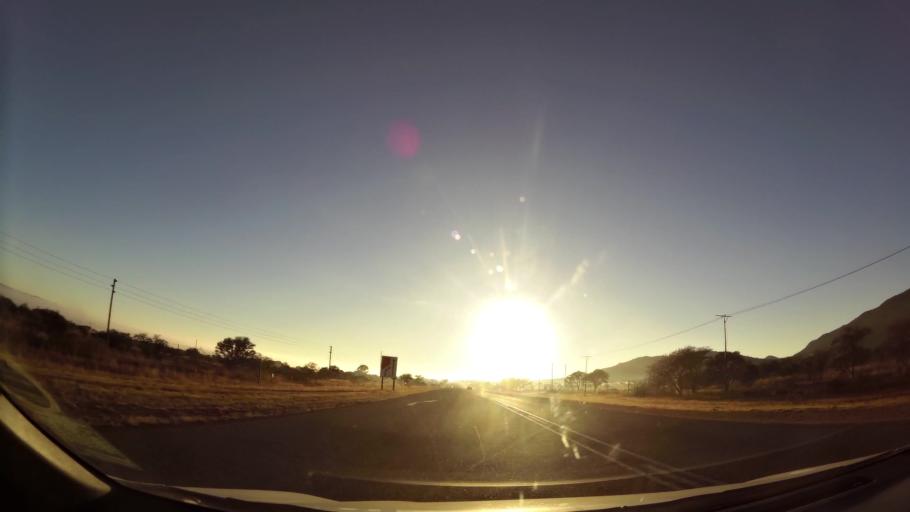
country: ZA
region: Limpopo
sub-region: Capricorn District Municipality
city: Polokwane
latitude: -24.0123
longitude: 29.3236
